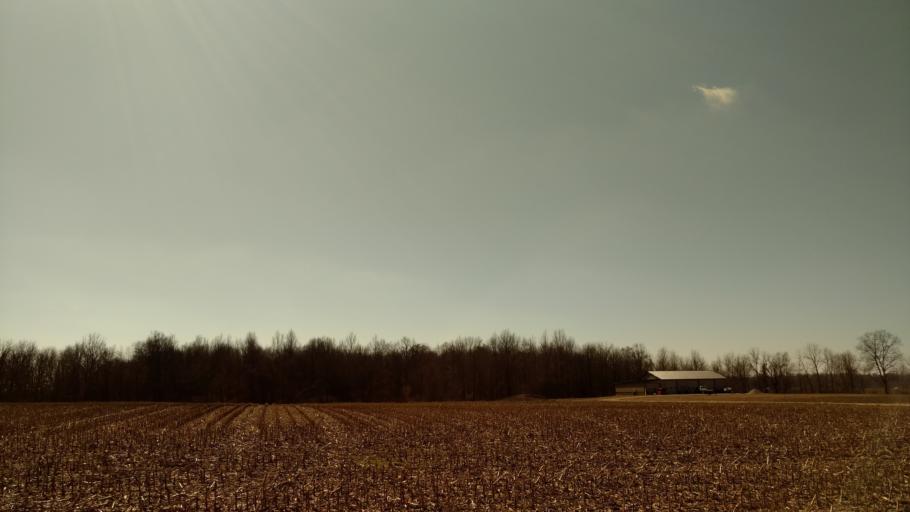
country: US
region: Ohio
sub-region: Morrow County
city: Cardington
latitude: 40.4978
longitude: -82.8582
